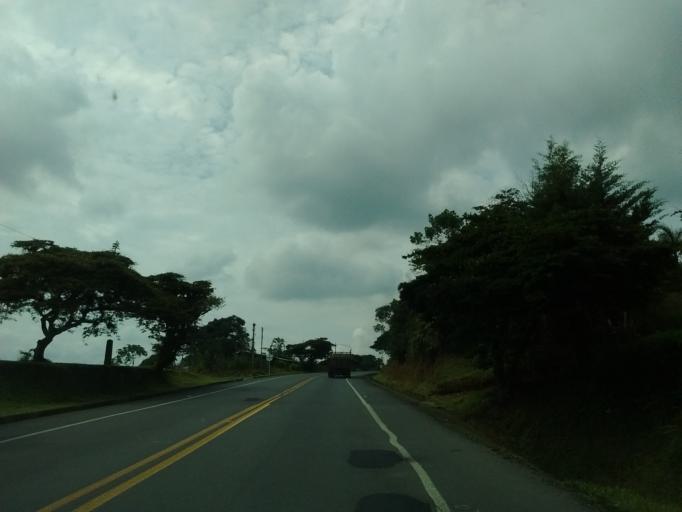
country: CO
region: Cauca
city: Morales
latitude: 2.7859
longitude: -76.5530
